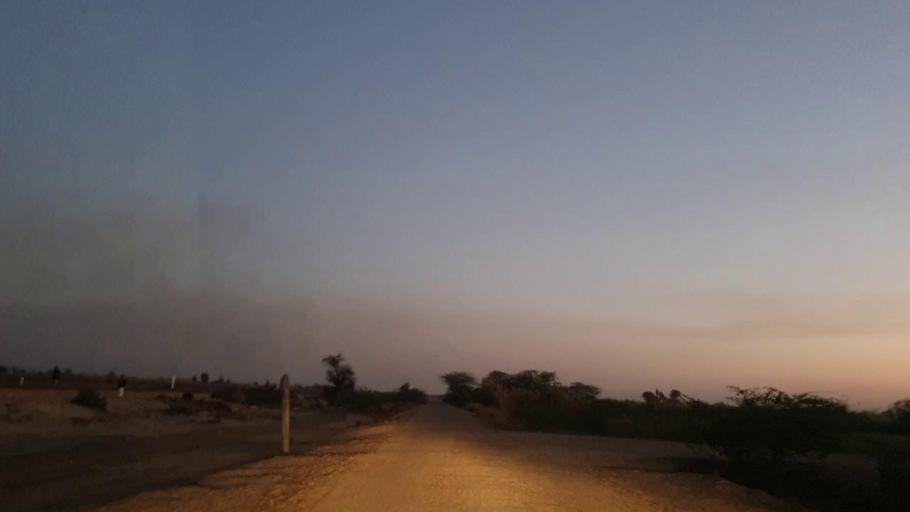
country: PK
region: Sindh
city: Nawabshah
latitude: 26.3383
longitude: 68.3720
